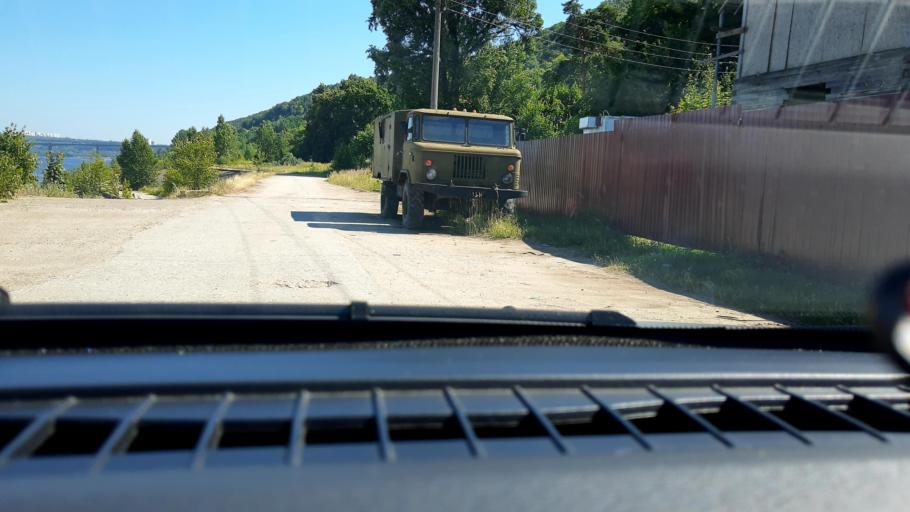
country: RU
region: Nizjnij Novgorod
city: Nizhniy Novgorod
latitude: 56.2318
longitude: 43.9253
